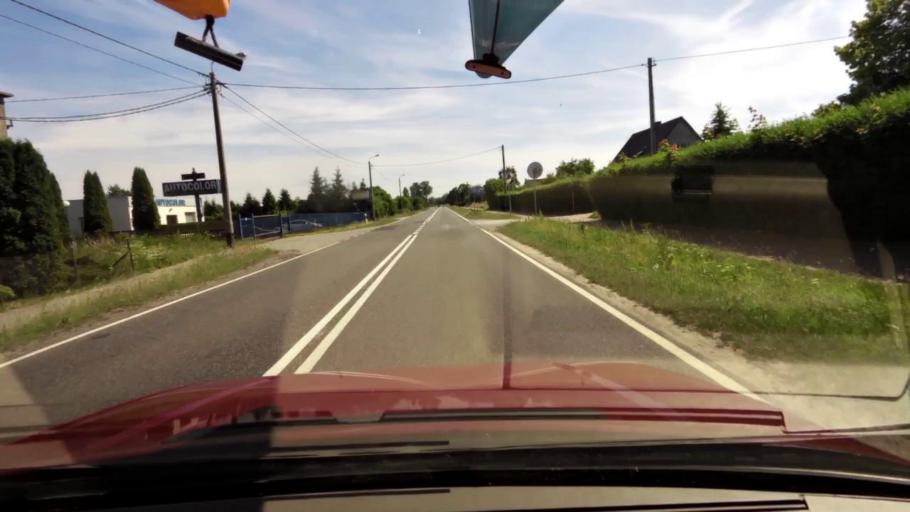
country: PL
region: Pomeranian Voivodeship
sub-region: Powiat slupski
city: Kobylnica
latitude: 54.4161
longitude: 17.0076
